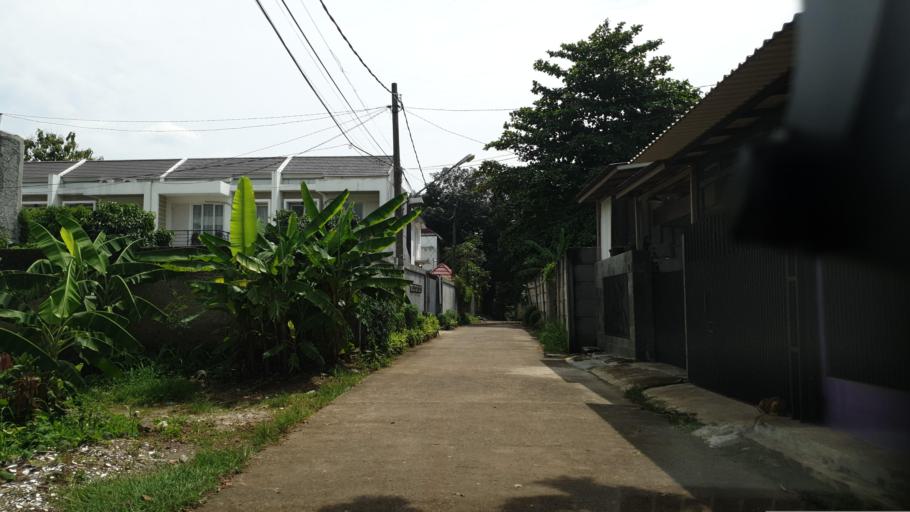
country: ID
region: West Java
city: Pamulang
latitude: -6.3637
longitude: 106.7662
